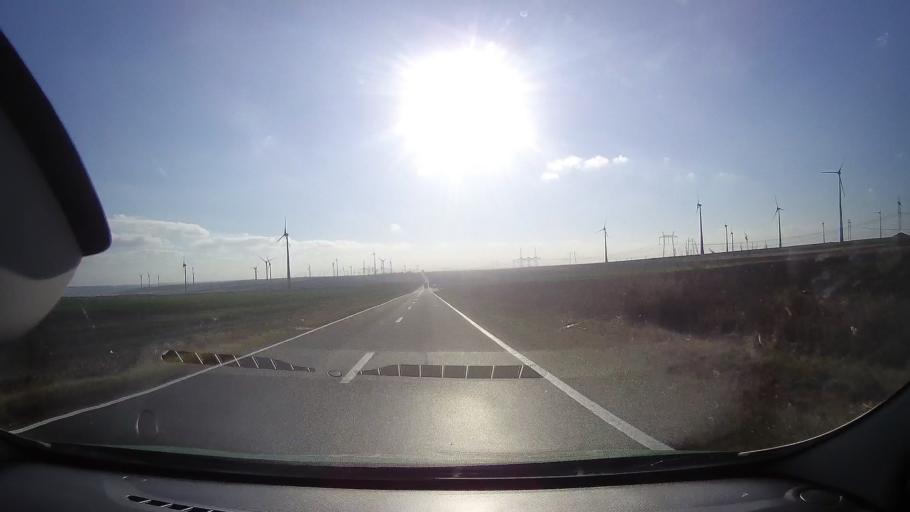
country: RO
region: Tulcea
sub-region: Comuna Topolog
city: Topolog
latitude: 44.8151
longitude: 28.2572
